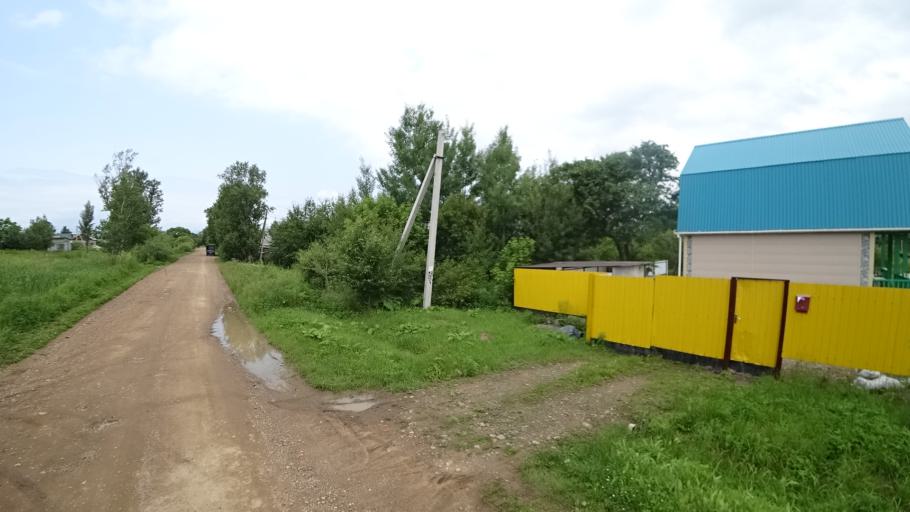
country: RU
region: Primorskiy
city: Novosysoyevka
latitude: 44.2276
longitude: 133.3674
